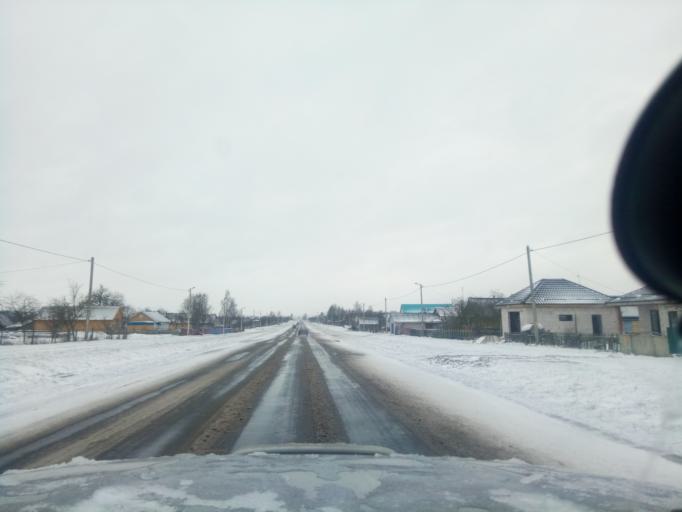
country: BY
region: Minsk
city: Klyetsk
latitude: 53.0305
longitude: 26.6552
